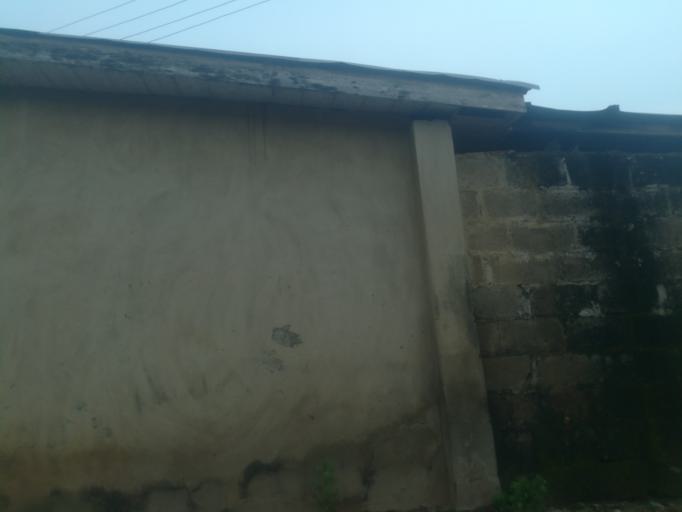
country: NG
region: Oyo
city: Ibadan
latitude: 7.3529
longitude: 3.8276
